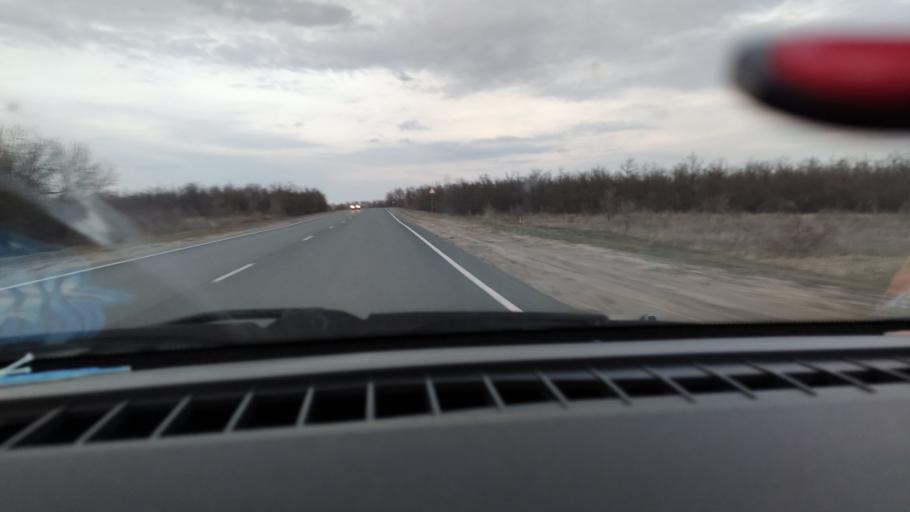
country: RU
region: Saratov
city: Sinodskoye
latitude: 51.9357
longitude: 46.5908
